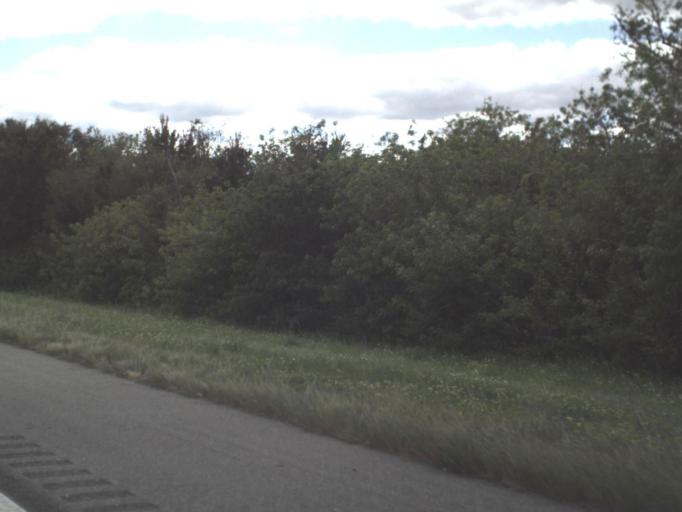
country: US
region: Florida
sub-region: Osceola County
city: Saint Cloud
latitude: 28.2488
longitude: -81.3290
